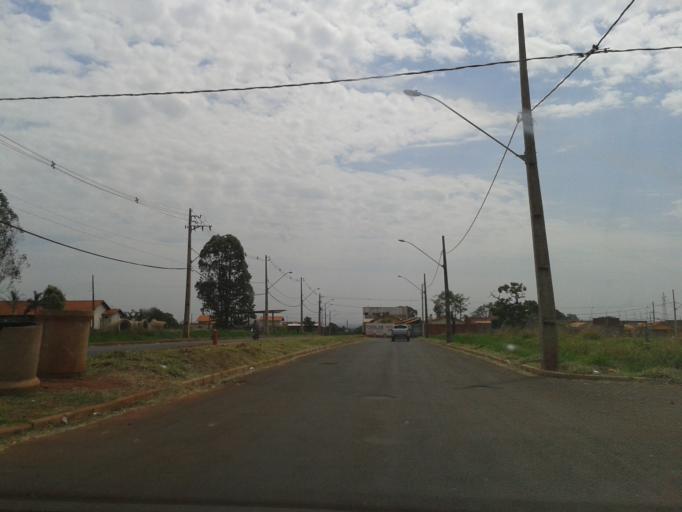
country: BR
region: Minas Gerais
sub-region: Ituiutaba
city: Ituiutaba
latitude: -18.9809
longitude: -49.4335
